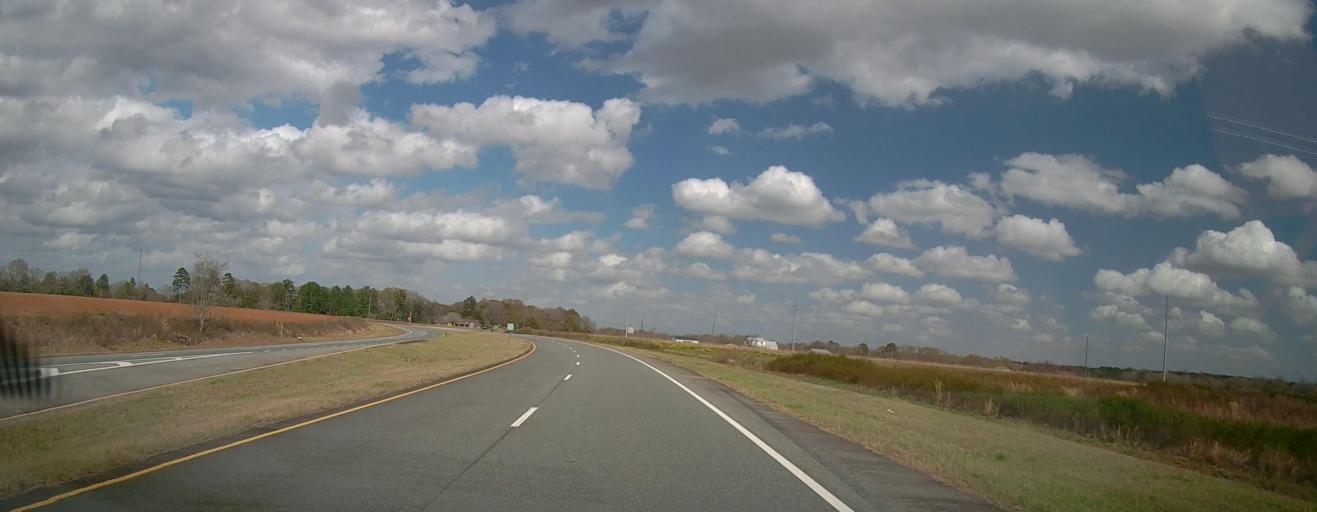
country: US
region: Georgia
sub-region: Houston County
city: Perry
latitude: 32.4306
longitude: -83.7238
